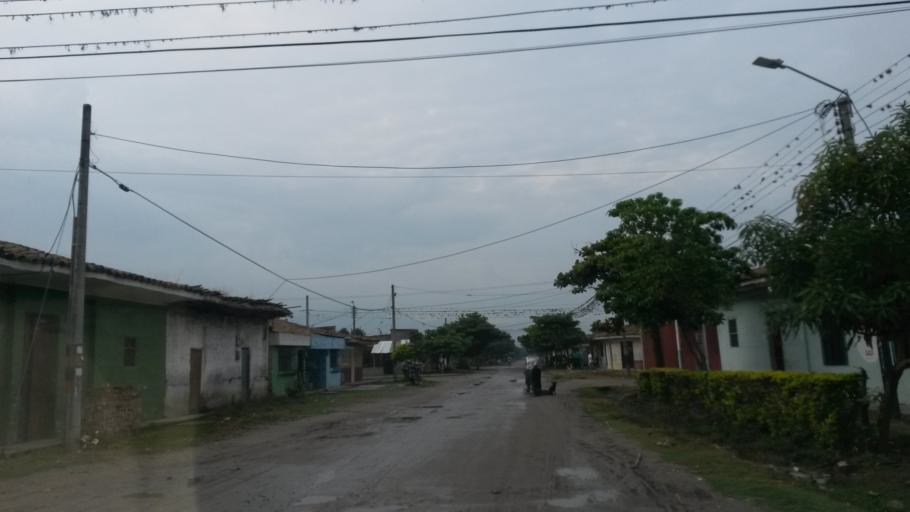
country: CO
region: Cauca
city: Padilla
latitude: 3.2244
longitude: -76.3146
